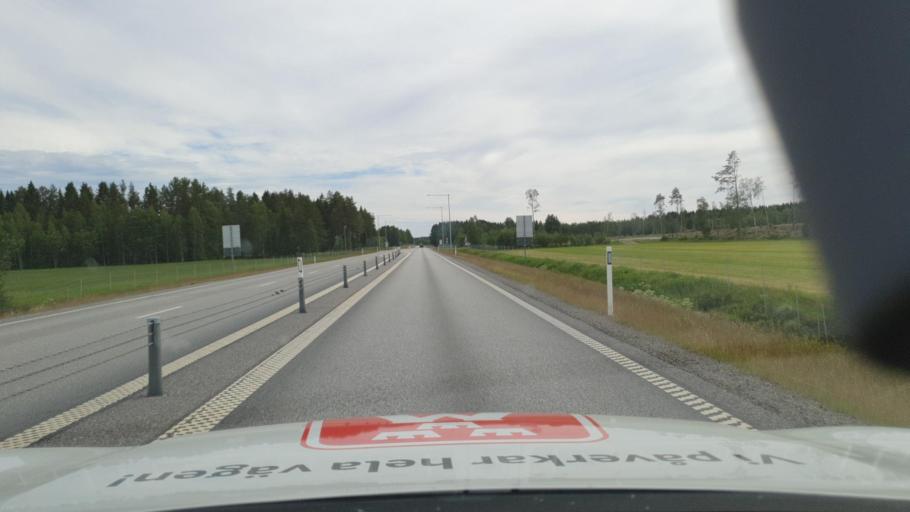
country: SE
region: Vaesterbotten
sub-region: Robertsfors Kommun
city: Robertsfors
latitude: 64.0925
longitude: 20.8690
